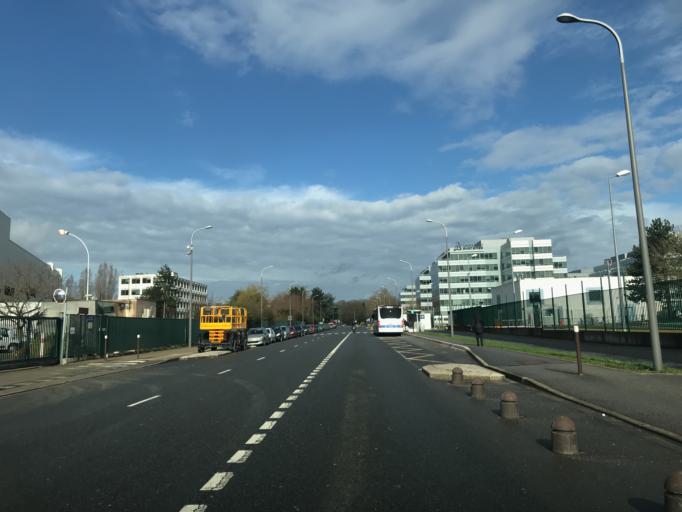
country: FR
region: Ile-de-France
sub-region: Departement des Yvelines
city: Velizy-Villacoublay
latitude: 48.7847
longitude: 2.2140
